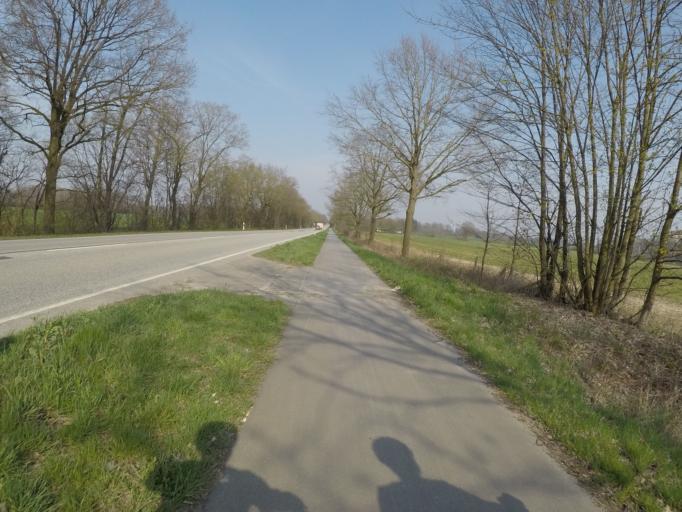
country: DE
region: Schleswig-Holstein
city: Seth
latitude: 53.8341
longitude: 10.2161
